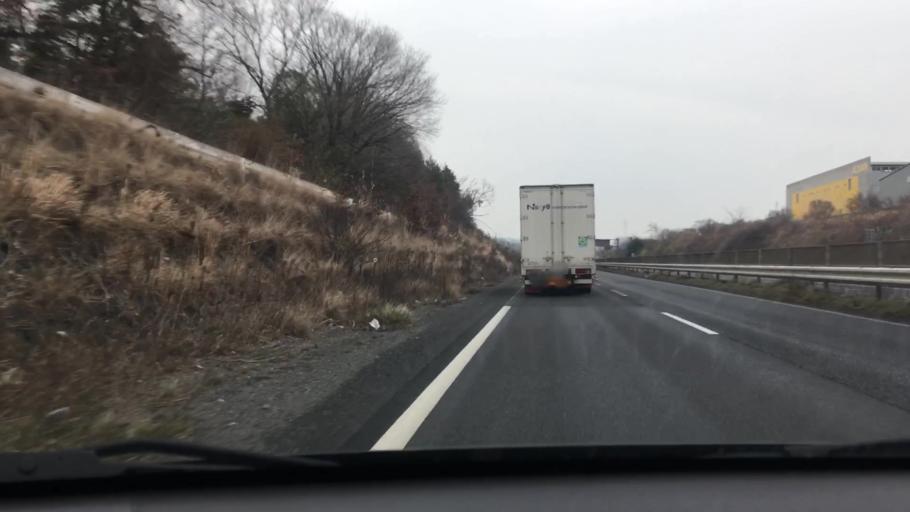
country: JP
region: Mie
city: Ueno-ebisumachi
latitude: 34.7110
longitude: 136.0782
